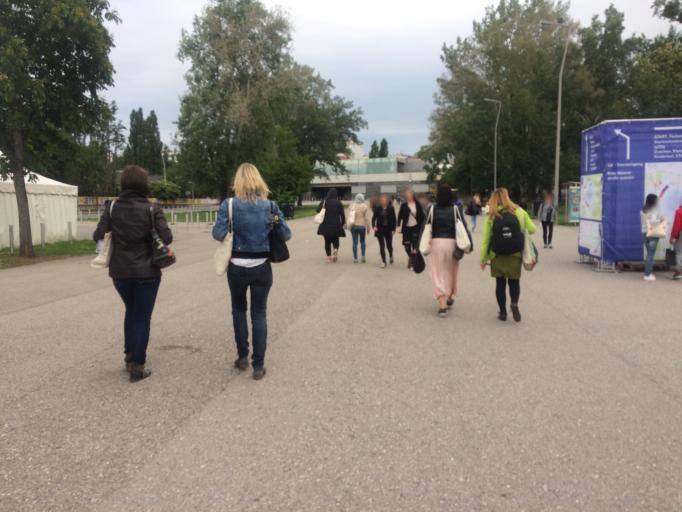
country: AT
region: Vienna
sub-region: Wien Stadt
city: Vienna
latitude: 48.2086
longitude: 16.4200
